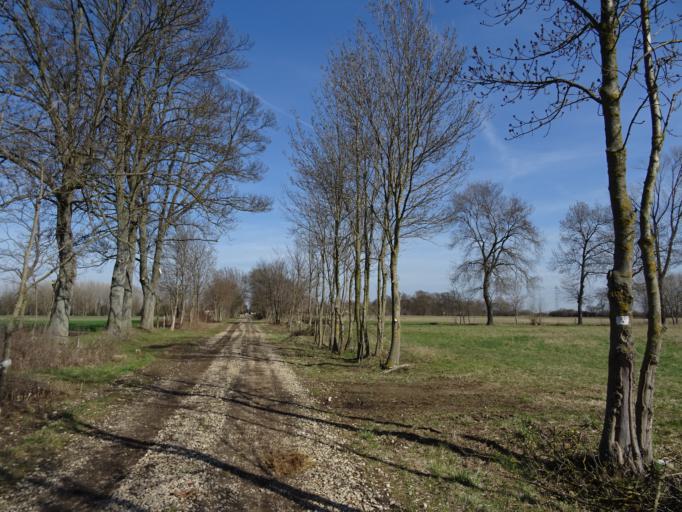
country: HU
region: Gyor-Moson-Sopron
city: Farad
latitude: 47.5475
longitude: 17.1751
